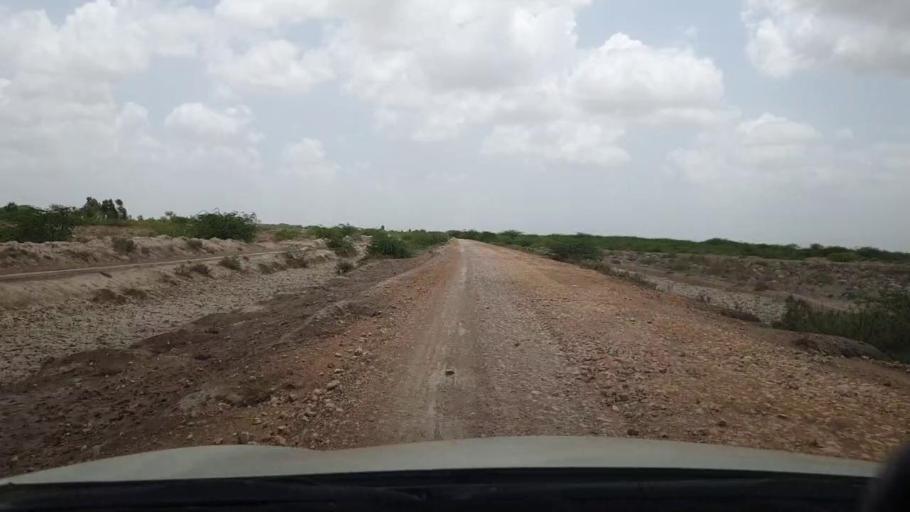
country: PK
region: Sindh
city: Kadhan
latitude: 24.3860
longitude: 68.9326
